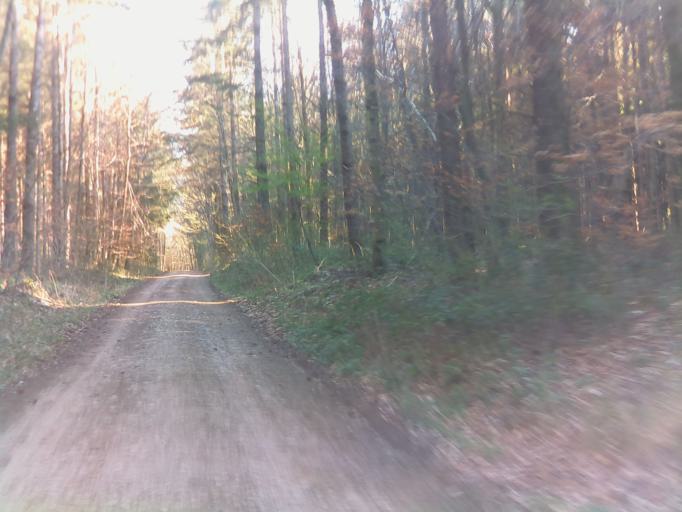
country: DE
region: Bavaria
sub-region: Swabia
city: Grossaitingen
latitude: 48.2494
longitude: 10.7525
